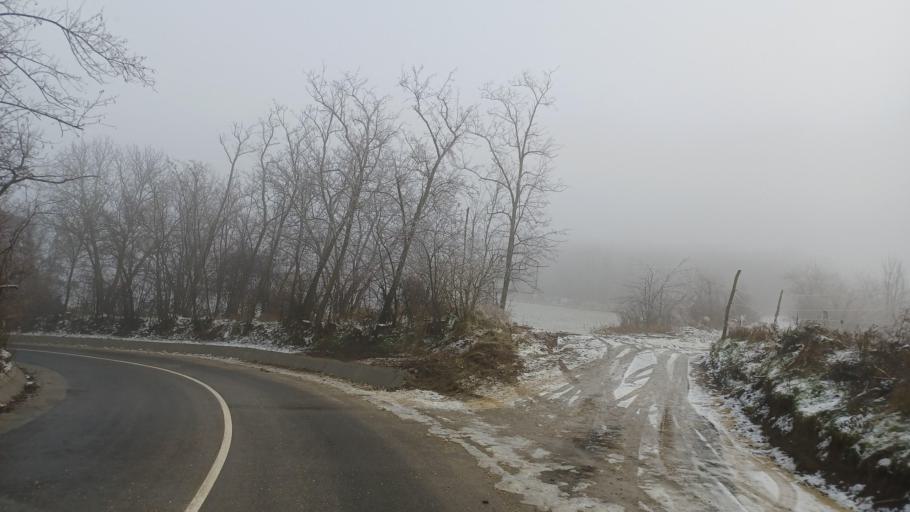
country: HU
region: Tolna
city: Gyonk
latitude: 46.5921
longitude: 18.4754
